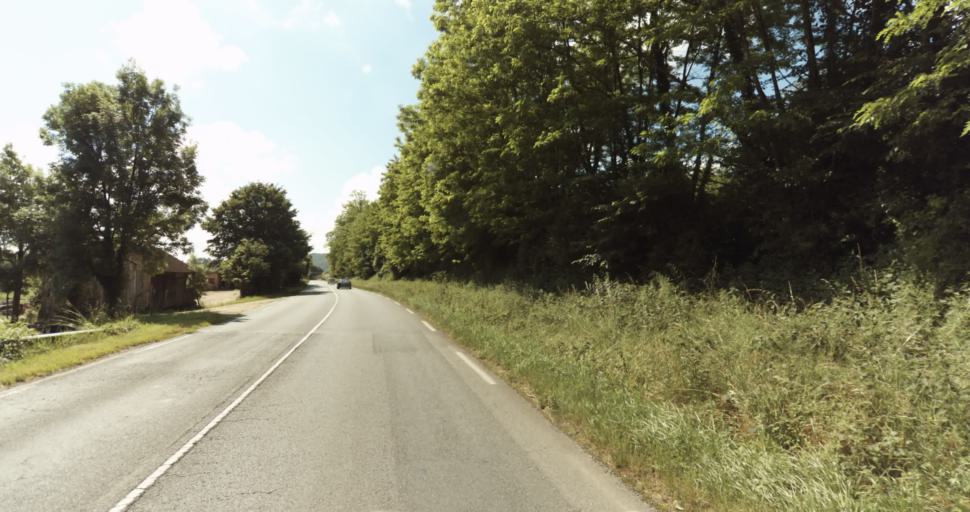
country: FR
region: Aquitaine
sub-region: Departement de la Dordogne
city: Le Bugue
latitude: 44.8378
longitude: 0.9348
